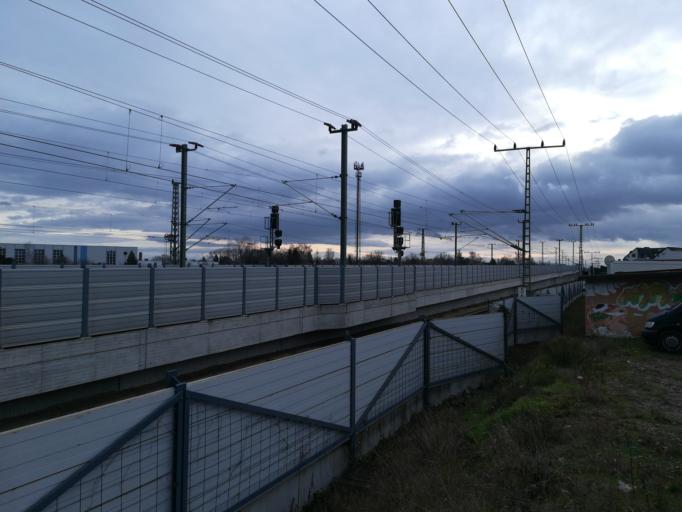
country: DE
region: Saxony-Anhalt
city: Schkopau
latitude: 51.4279
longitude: 11.9876
